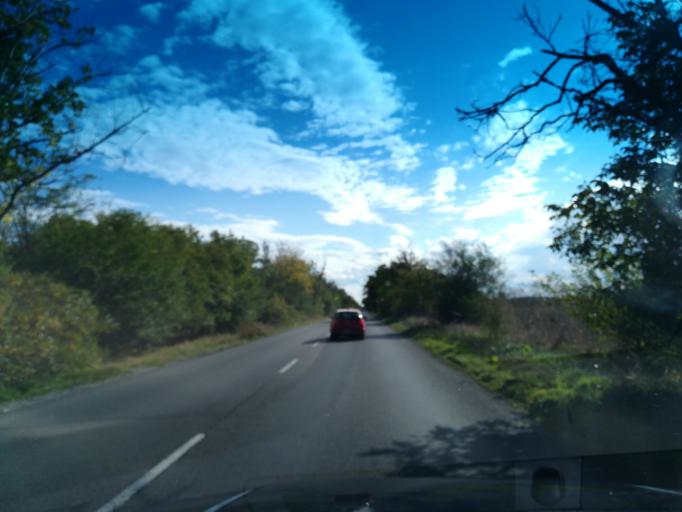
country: BG
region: Stara Zagora
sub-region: Obshtina Stara Zagora
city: Stara Zagora
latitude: 42.3721
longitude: 25.6527
